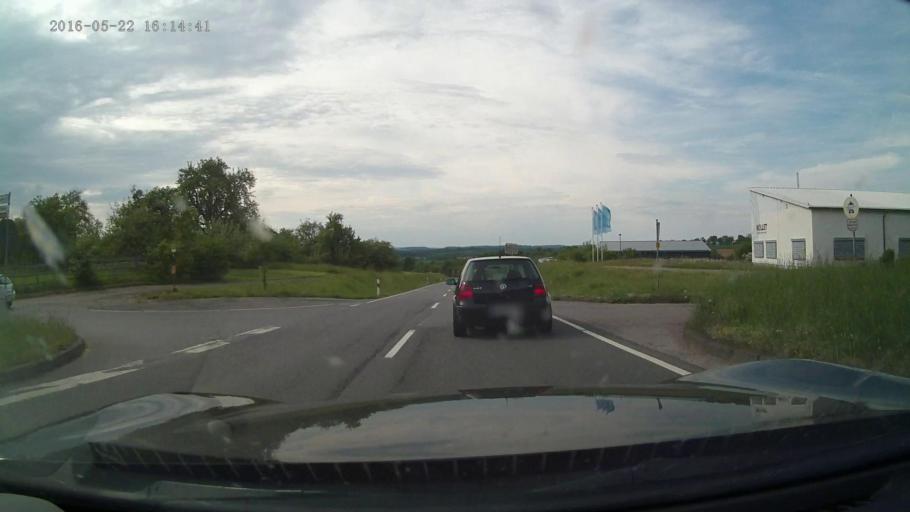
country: DE
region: Baden-Wuerttemberg
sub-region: Karlsruhe Region
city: Osterburken
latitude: 49.4224
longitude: 9.4428
